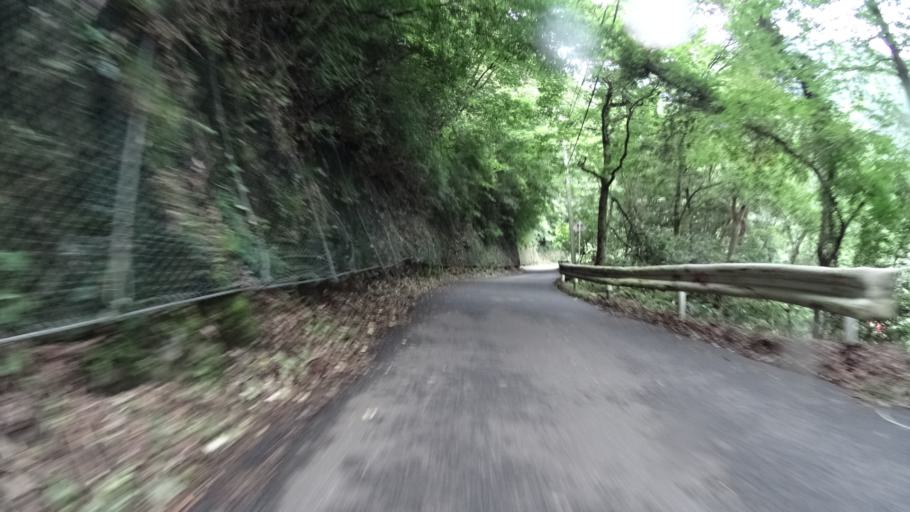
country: JP
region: Kanagawa
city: Hadano
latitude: 35.4869
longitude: 139.2204
